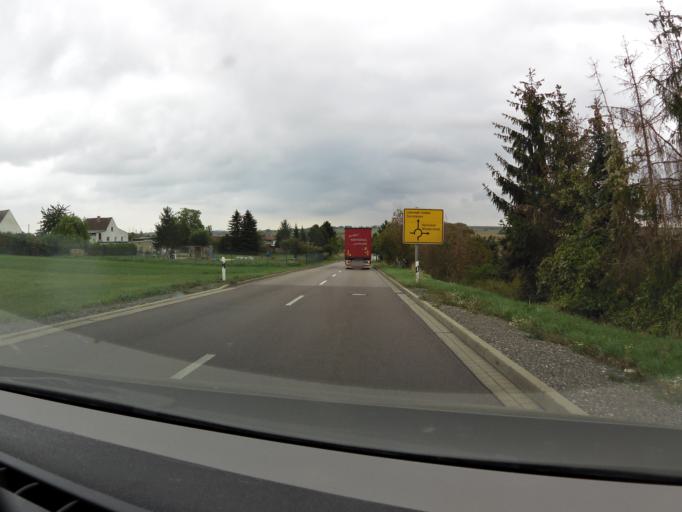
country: DE
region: Saxony-Anhalt
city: Sandersleben
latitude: 51.6784
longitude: 11.5770
